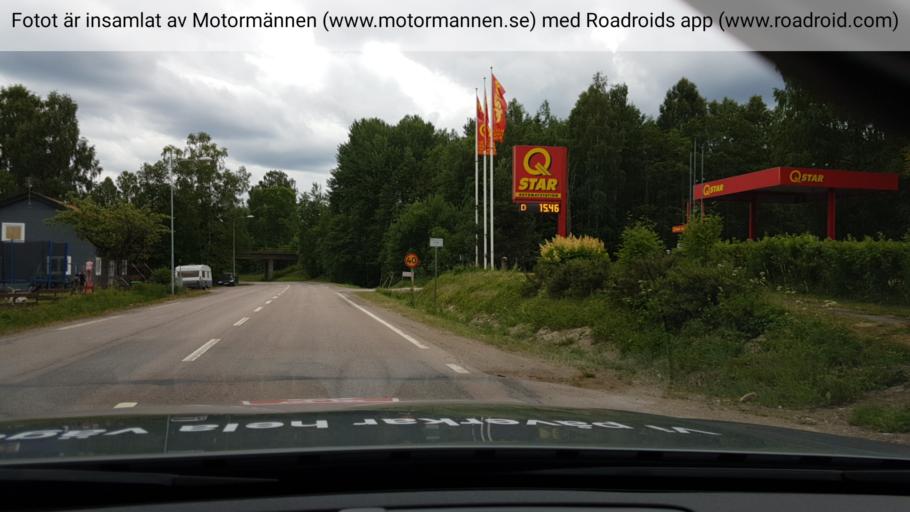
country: SE
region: Vaestmanland
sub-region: Skinnskattebergs Kommun
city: Skinnskatteberg
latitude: 59.8314
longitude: 15.6767
